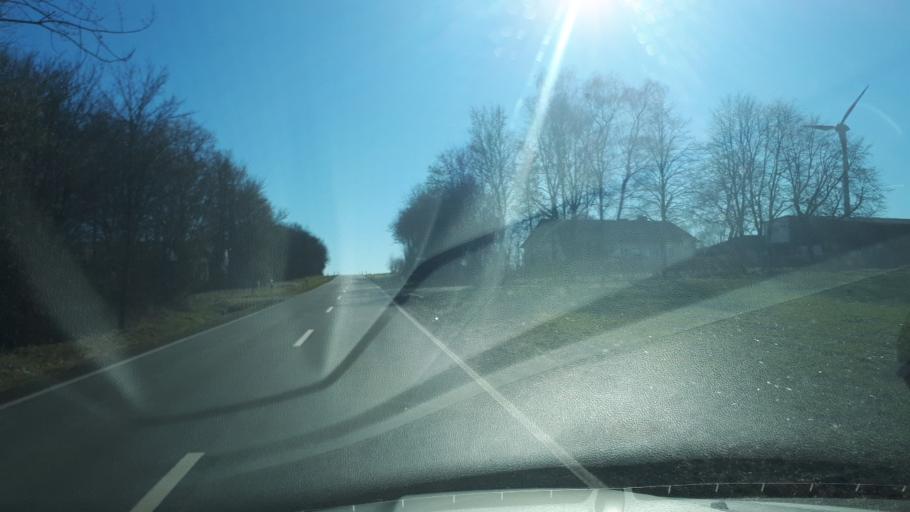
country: DE
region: Rheinland-Pfalz
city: Muckeln
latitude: 50.0945
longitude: 6.9157
